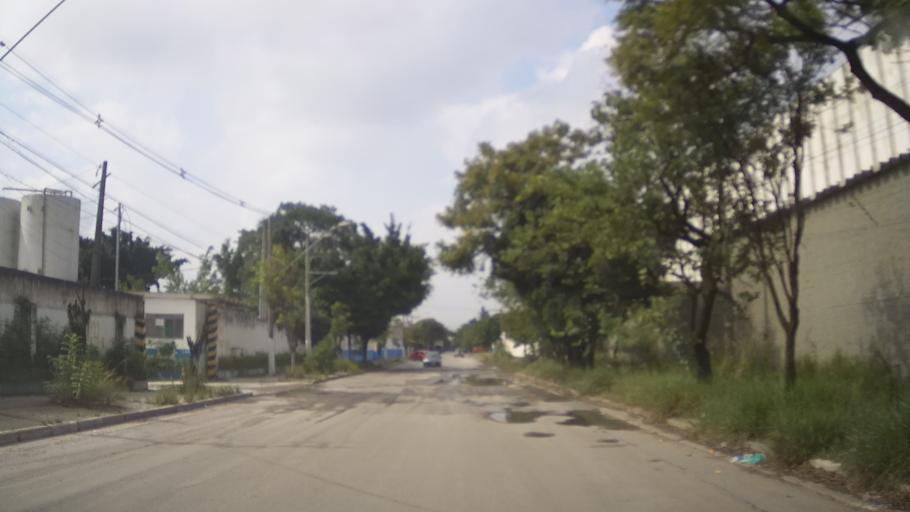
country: BR
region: Sao Paulo
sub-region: Guarulhos
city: Guarulhos
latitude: -23.4770
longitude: -46.4707
